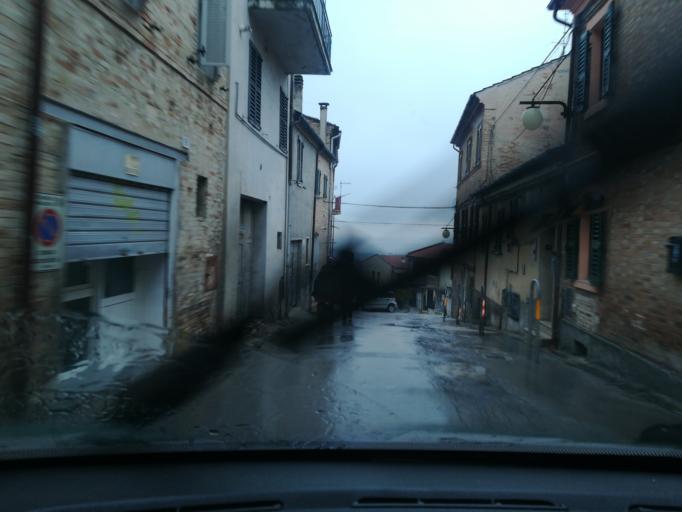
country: IT
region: The Marches
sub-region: Provincia di Macerata
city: Macerata
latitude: 43.3015
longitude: 13.4575
